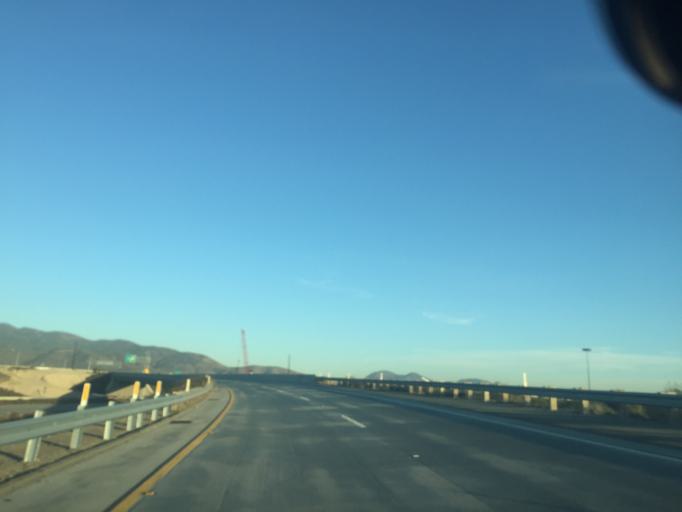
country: MX
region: Baja California
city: Tijuana
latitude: 32.5635
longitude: -116.9516
